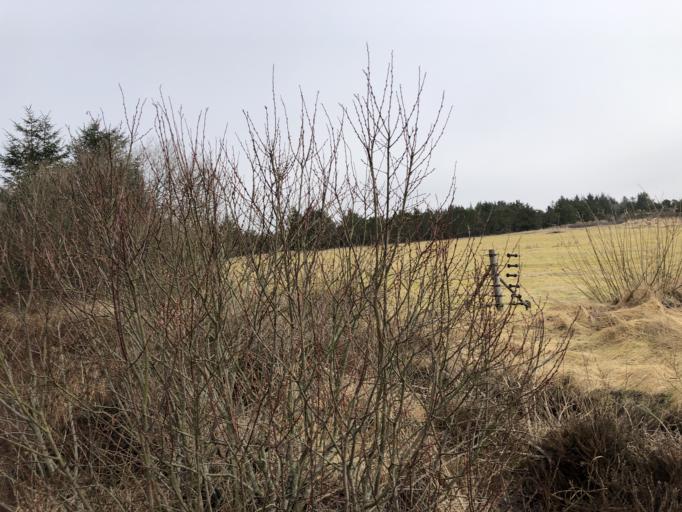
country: DK
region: Central Jutland
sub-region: Holstebro Kommune
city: Ulfborg
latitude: 56.3142
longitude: 8.1374
